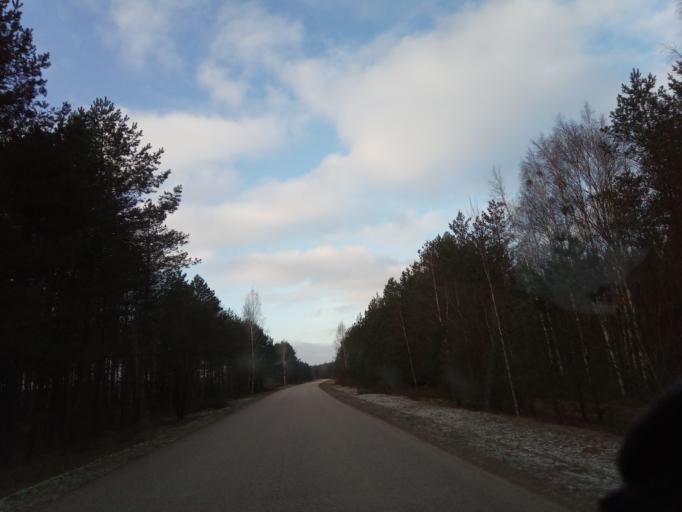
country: LT
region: Alytaus apskritis
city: Druskininkai
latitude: 53.9770
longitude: 24.2482
